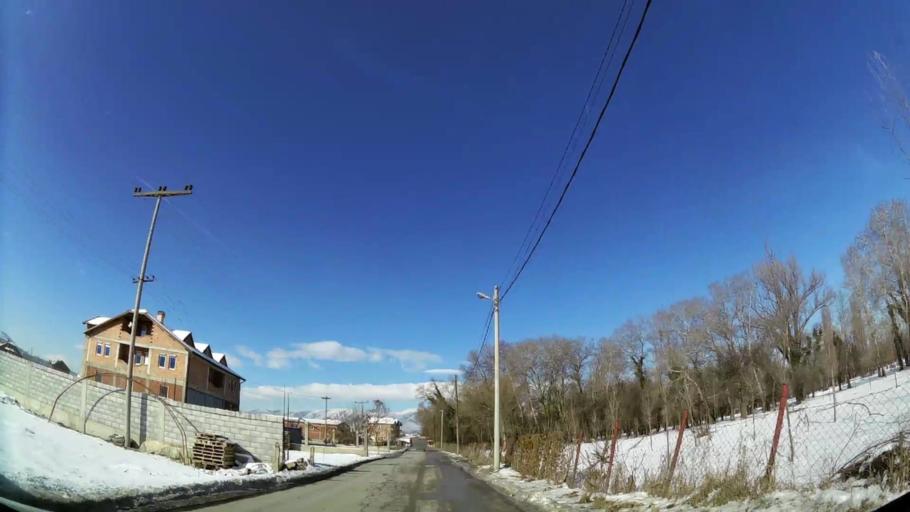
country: MK
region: Saraj
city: Saraj
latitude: 41.9996
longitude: 21.3399
